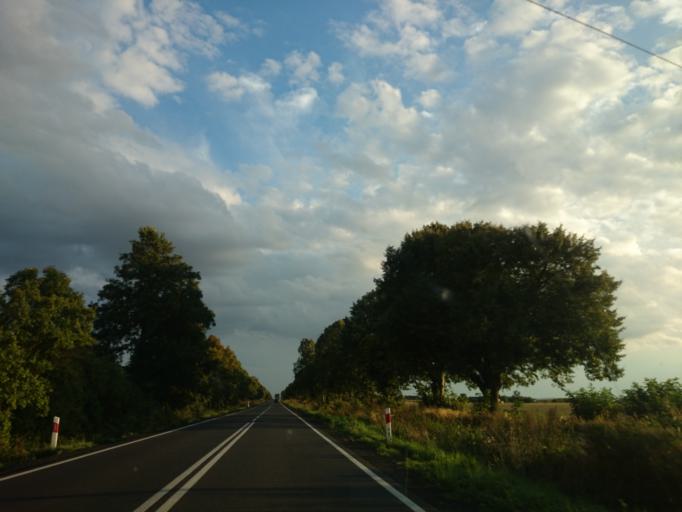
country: PL
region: West Pomeranian Voivodeship
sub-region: Powiat mysliborski
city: Debno
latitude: 52.6821
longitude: 14.6848
